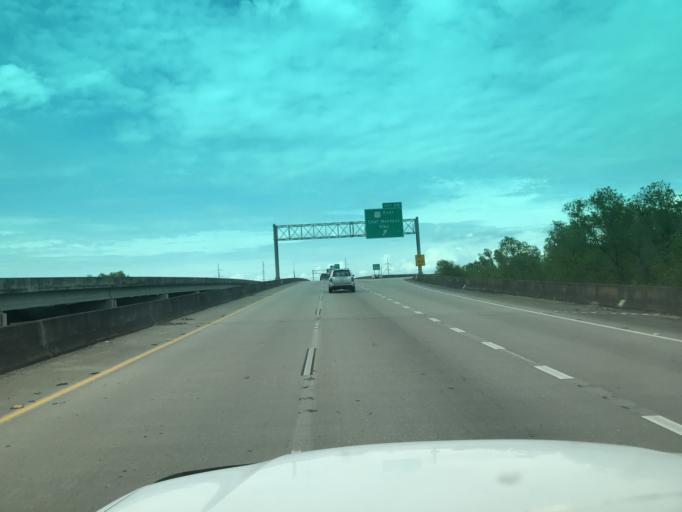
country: US
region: Louisiana
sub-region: Saint Bernard Parish
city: Chalmette
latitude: 30.0234
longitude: -89.9393
